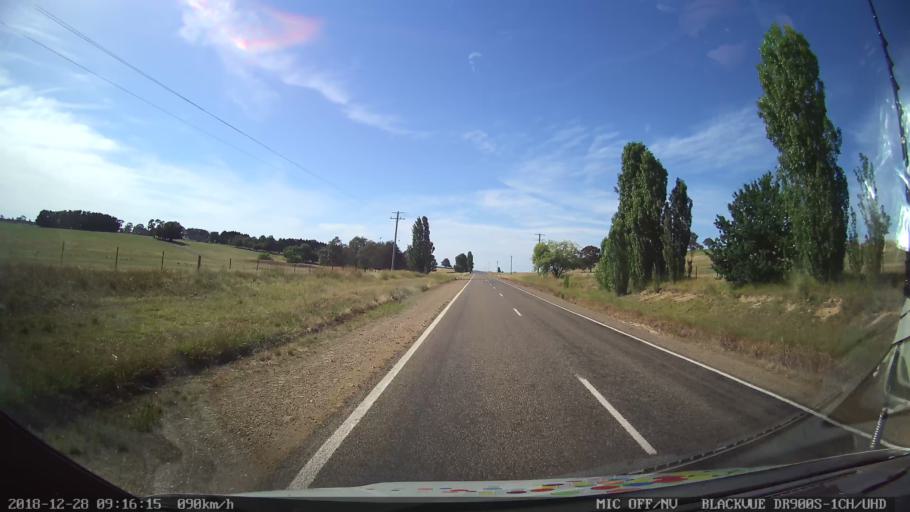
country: AU
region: New South Wales
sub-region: Upper Lachlan Shire
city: Crookwell
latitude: -34.3060
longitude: 149.3546
